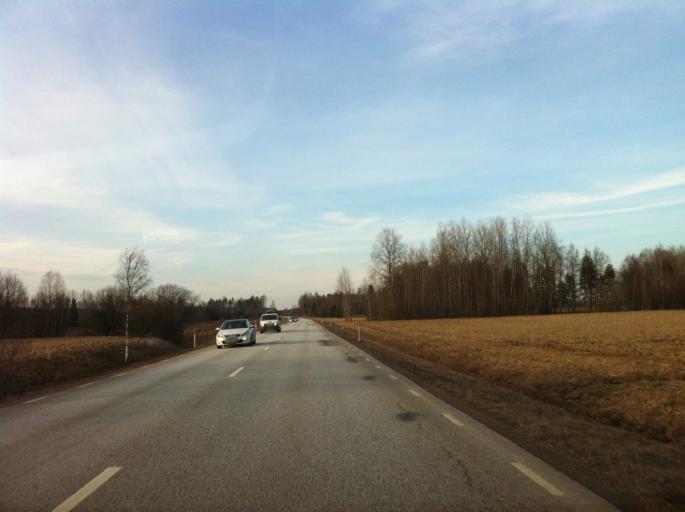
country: SE
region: Vaermland
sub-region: Storfors Kommun
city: Storfors
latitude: 59.5560
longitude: 14.2732
